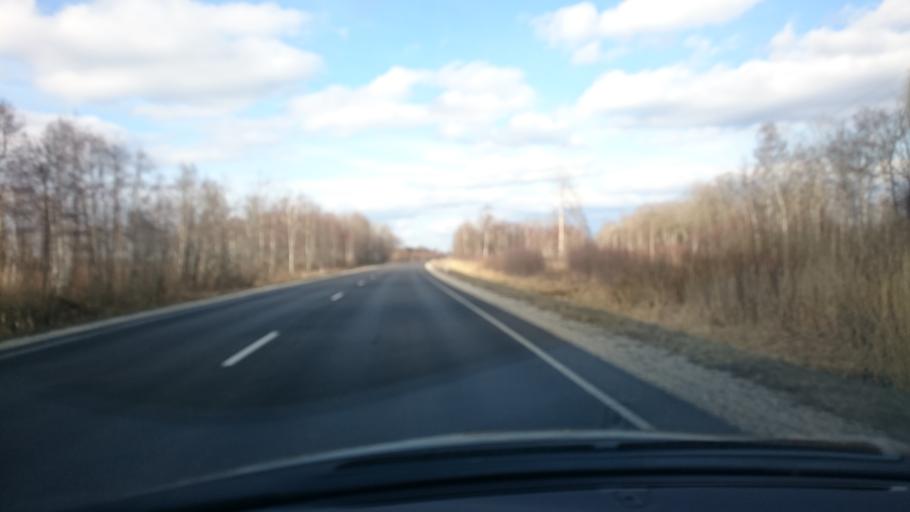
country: EE
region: Laeaene
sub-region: Lihula vald
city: Lihula
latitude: 58.8418
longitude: 24.0592
